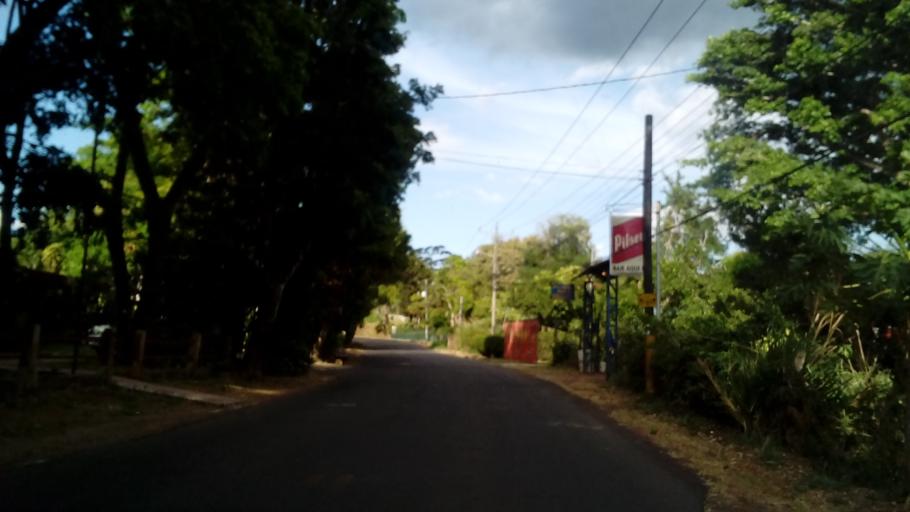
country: CR
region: Alajuela
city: Sabanilla
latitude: 10.0817
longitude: -84.2644
